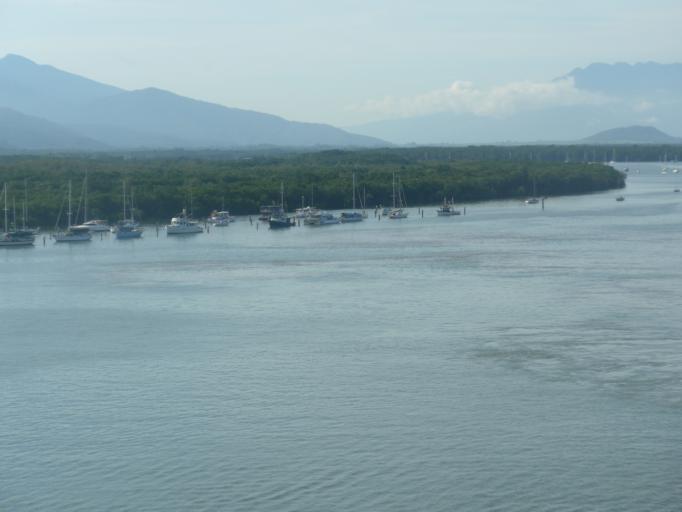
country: AU
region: Queensland
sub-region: Cairns
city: Cairns
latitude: -16.9262
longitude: 145.7808
